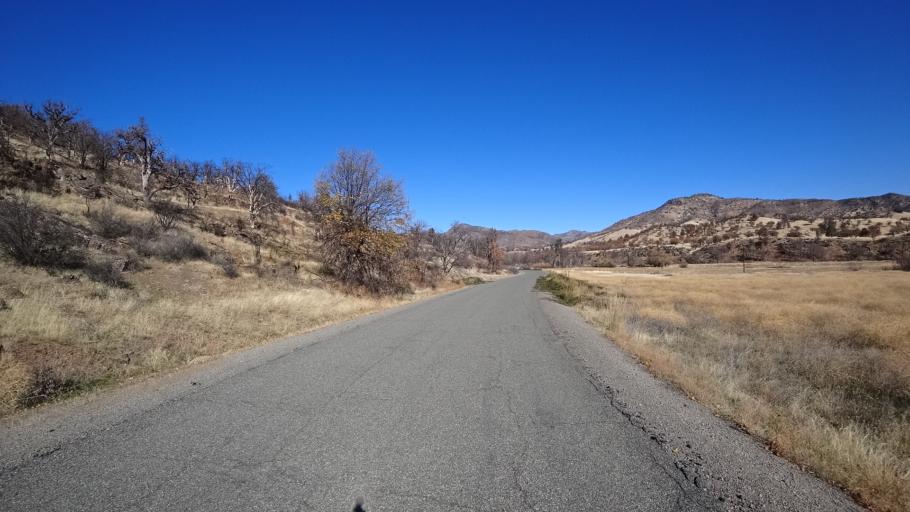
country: US
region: California
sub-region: Siskiyou County
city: Yreka
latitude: 41.9340
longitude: -122.5926
